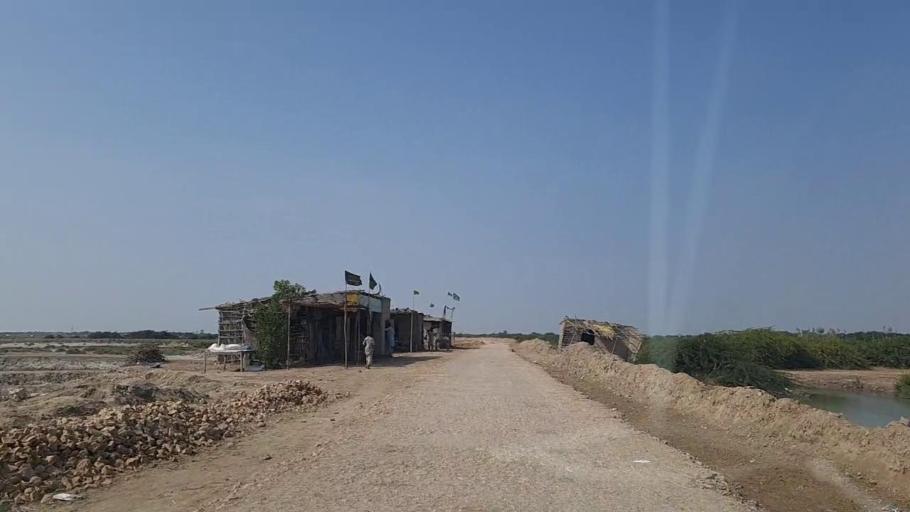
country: PK
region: Sindh
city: Chuhar Jamali
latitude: 24.1960
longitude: 67.8377
